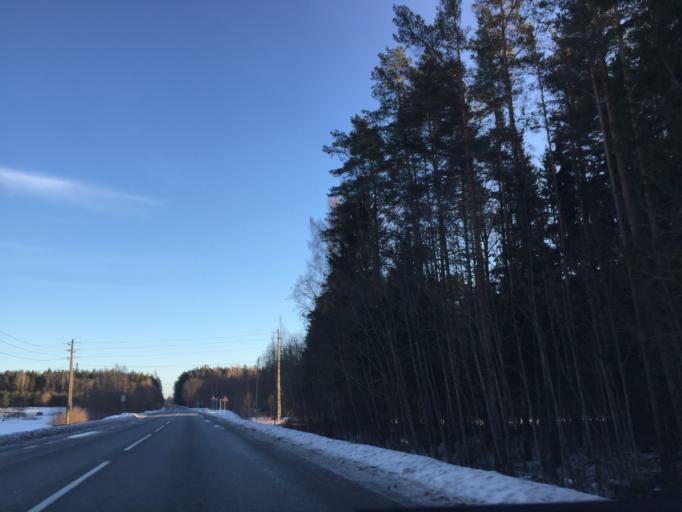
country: LV
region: Ogre
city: Jumprava
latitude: 56.6334
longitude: 24.9058
